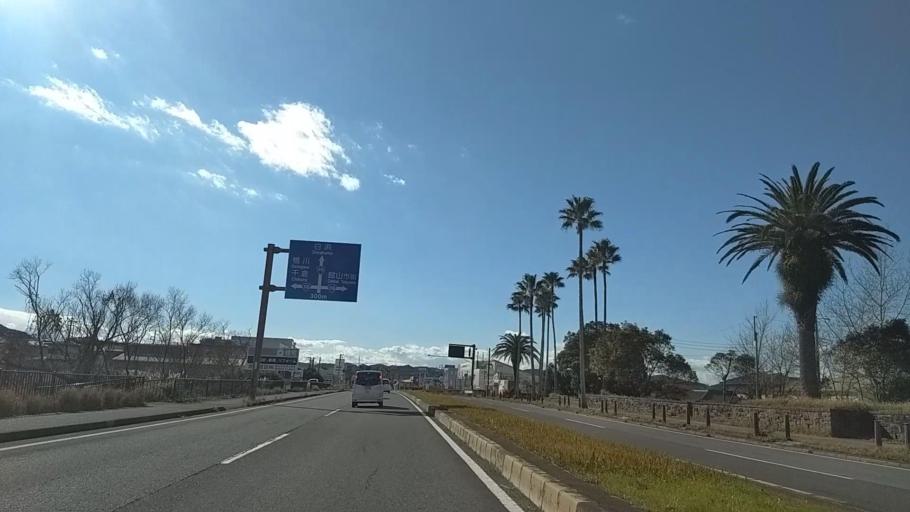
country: JP
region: Chiba
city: Tateyama
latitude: 34.9946
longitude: 139.8743
